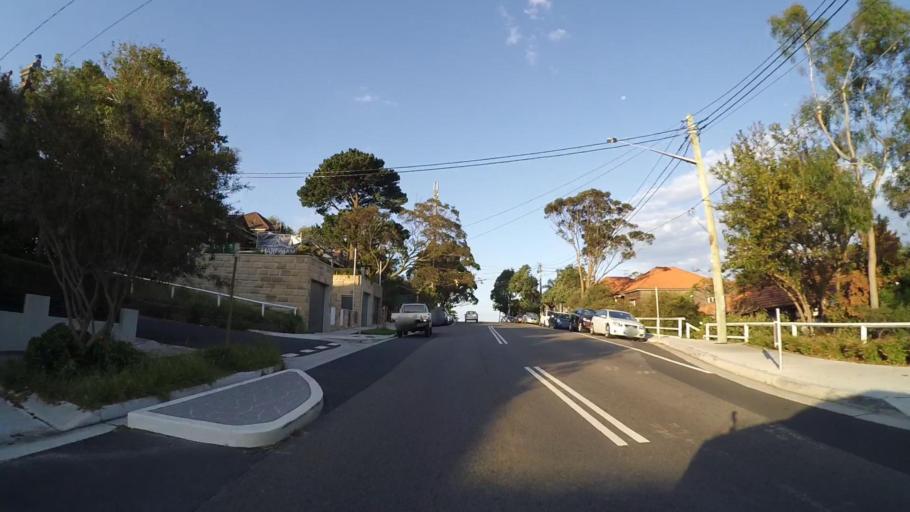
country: AU
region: New South Wales
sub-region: Randwick
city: Randwick
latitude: -33.9226
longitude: 151.2455
